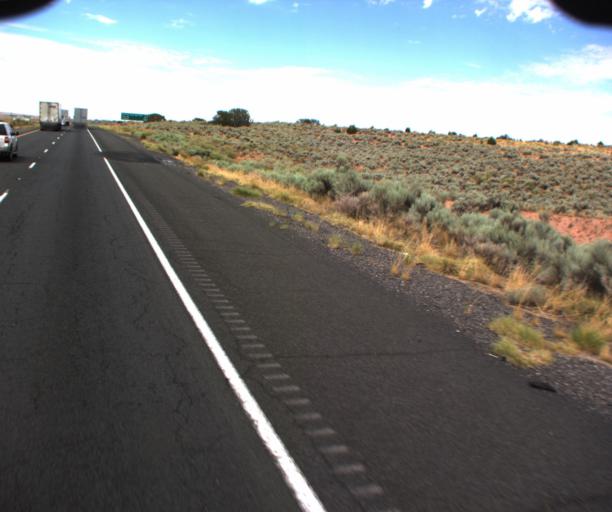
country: US
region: Arizona
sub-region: Apache County
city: Houck
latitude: 35.1577
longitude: -109.4968
